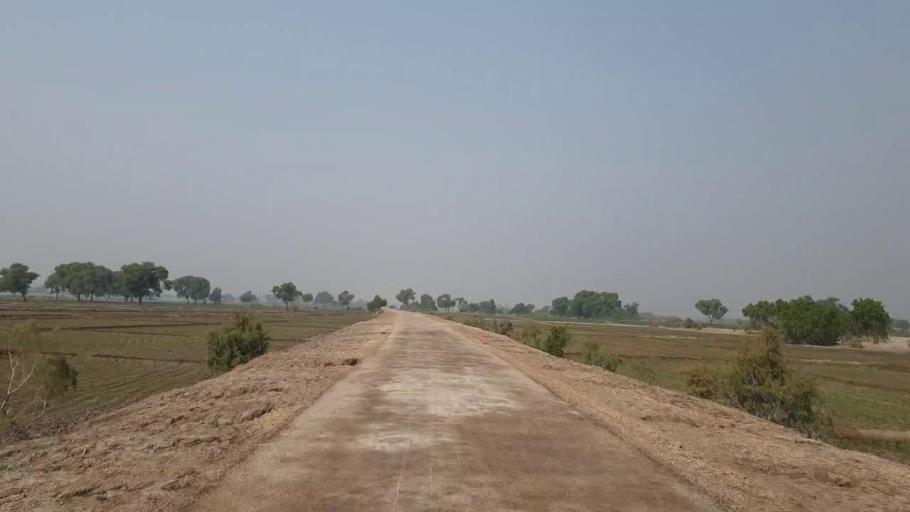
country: PK
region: Sindh
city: Bhan
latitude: 26.4971
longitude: 67.6977
